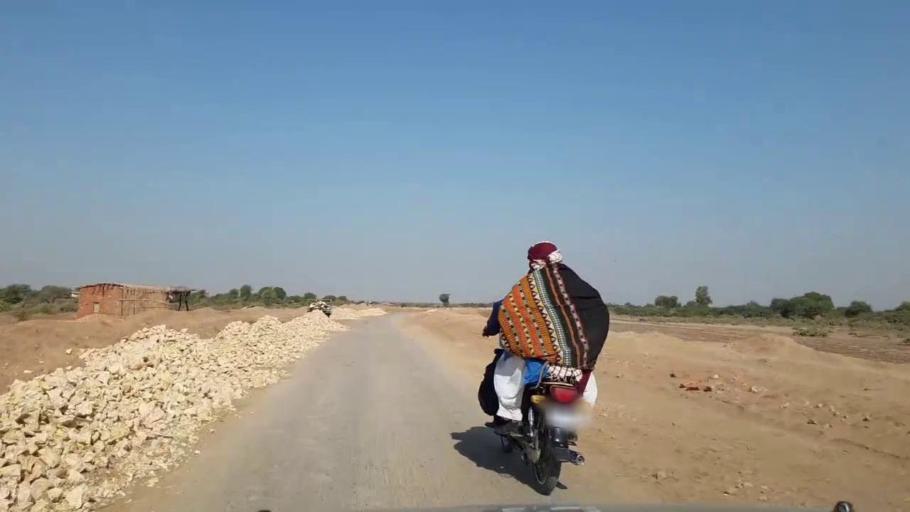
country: PK
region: Sindh
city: Digri
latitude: 24.9651
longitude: 69.1126
